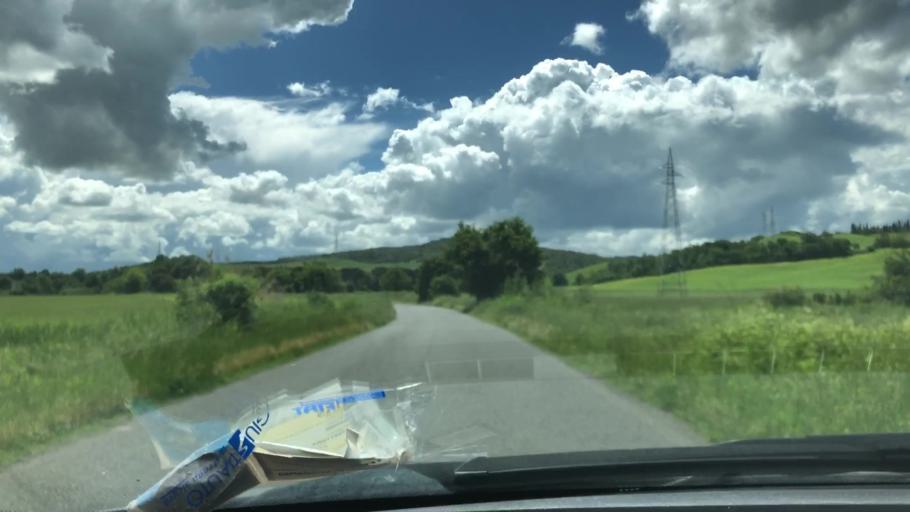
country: IT
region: Tuscany
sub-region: Province of Pisa
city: Saline
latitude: 43.3520
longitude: 10.7880
